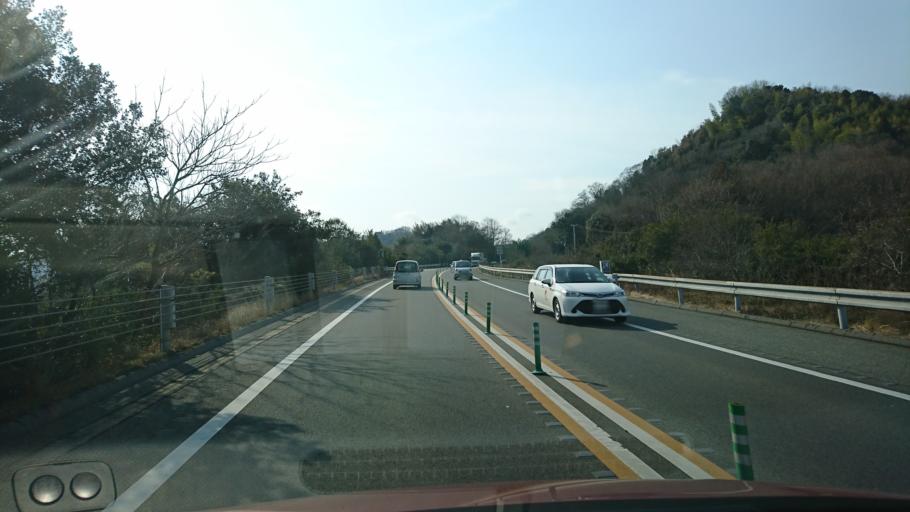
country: JP
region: Hiroshima
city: Onomichi
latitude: 34.3902
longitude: 133.2058
